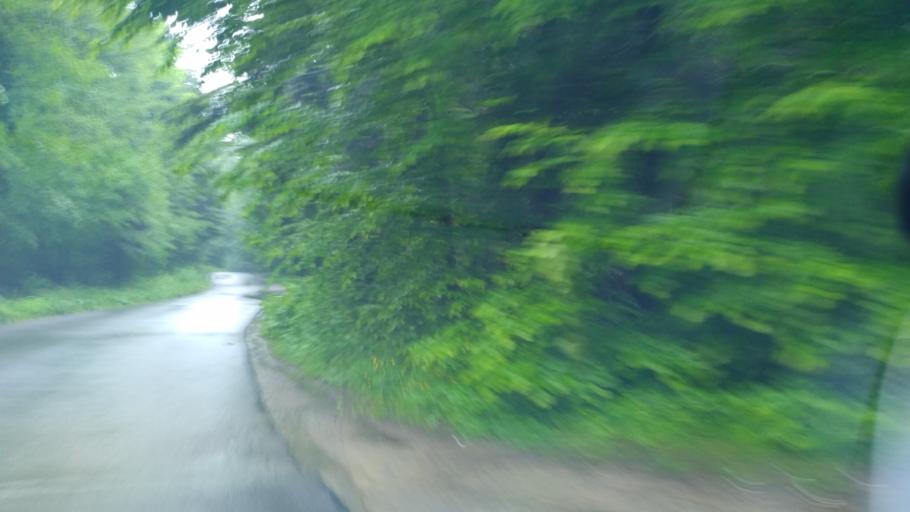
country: PL
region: Subcarpathian Voivodeship
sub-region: Powiat jasielski
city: Jaslo
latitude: 49.7749
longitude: 21.4922
